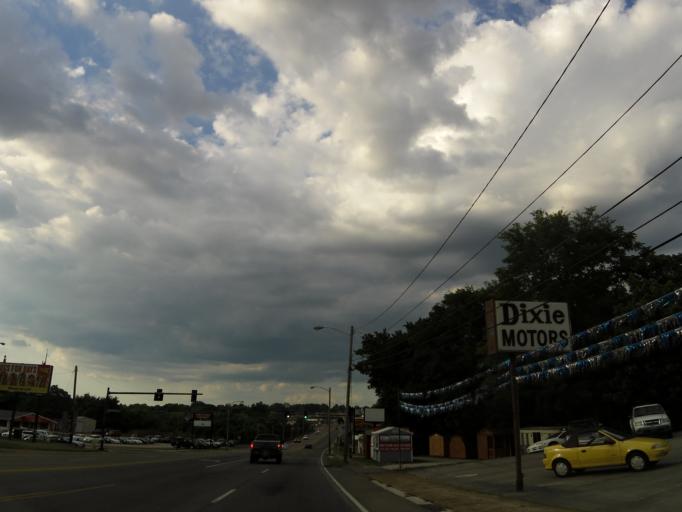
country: US
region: Tennessee
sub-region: Maury County
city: Columbia
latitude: 35.6206
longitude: -87.0346
